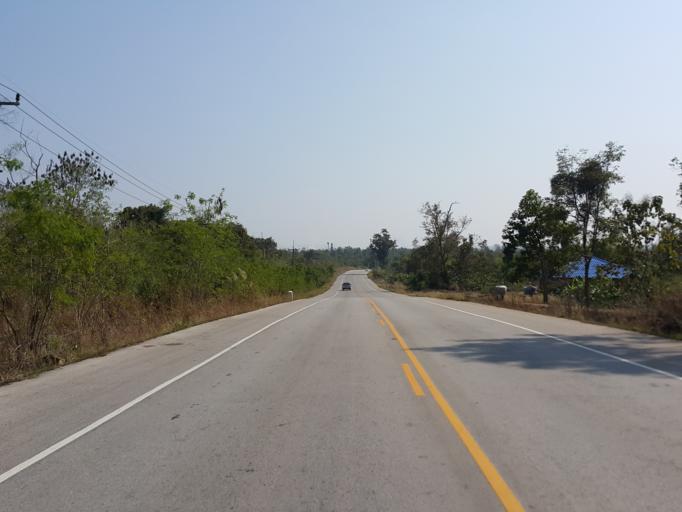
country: TH
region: Lampang
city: Mueang Pan
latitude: 18.9406
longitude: 99.6095
